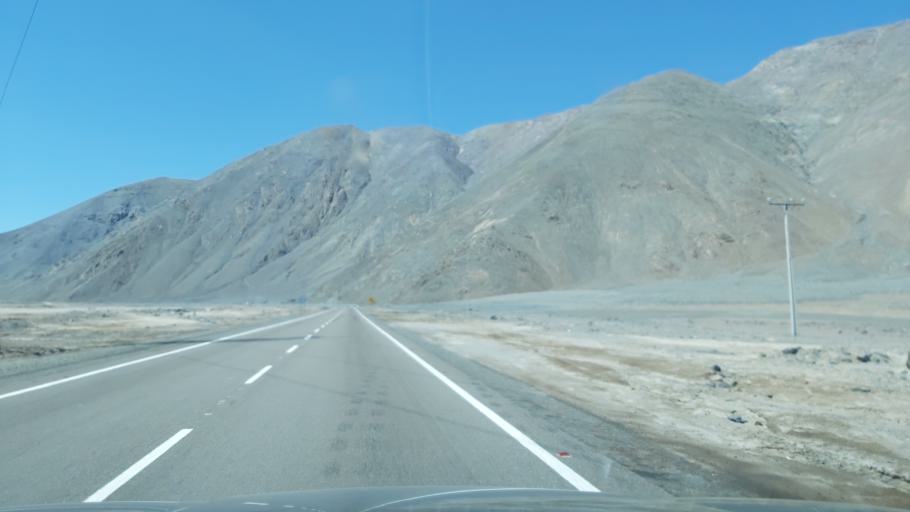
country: CL
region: Atacama
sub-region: Provincia de Chanaral
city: Diego de Almagro
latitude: -26.3449
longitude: -69.7435
